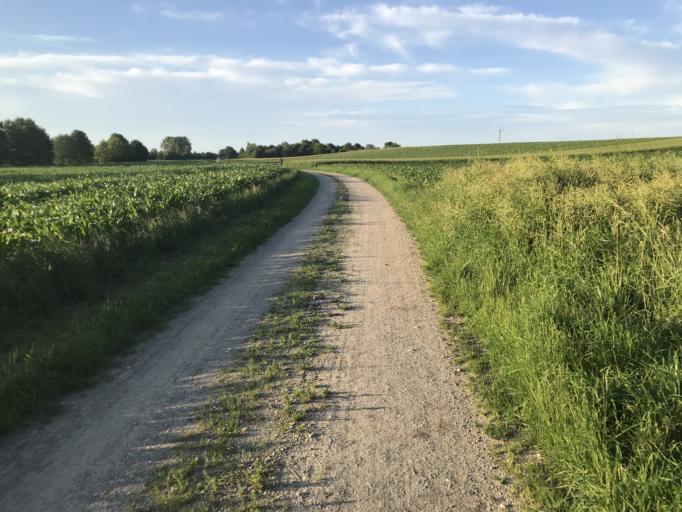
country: DE
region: Bavaria
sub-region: Swabia
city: Merching
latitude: 48.2530
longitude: 10.9660
